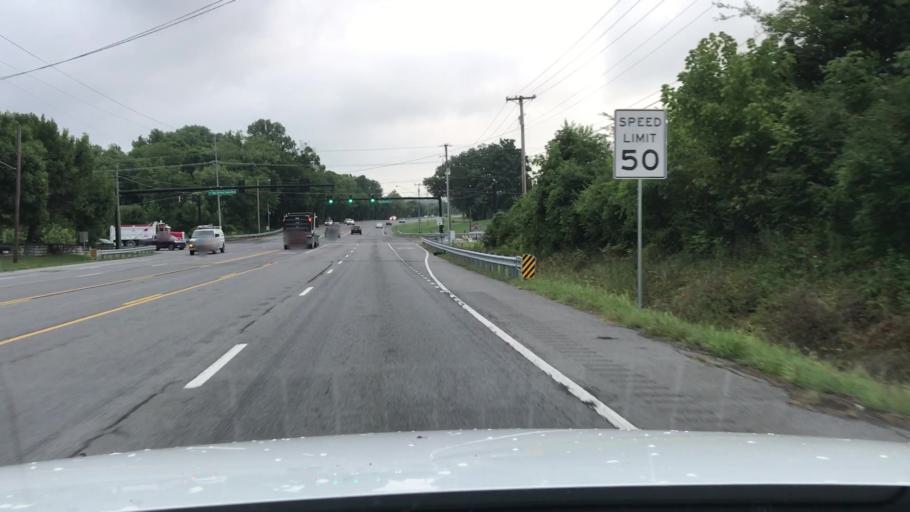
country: US
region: Tennessee
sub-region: Sumner County
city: Gallatin
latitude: 36.3455
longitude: -86.5257
